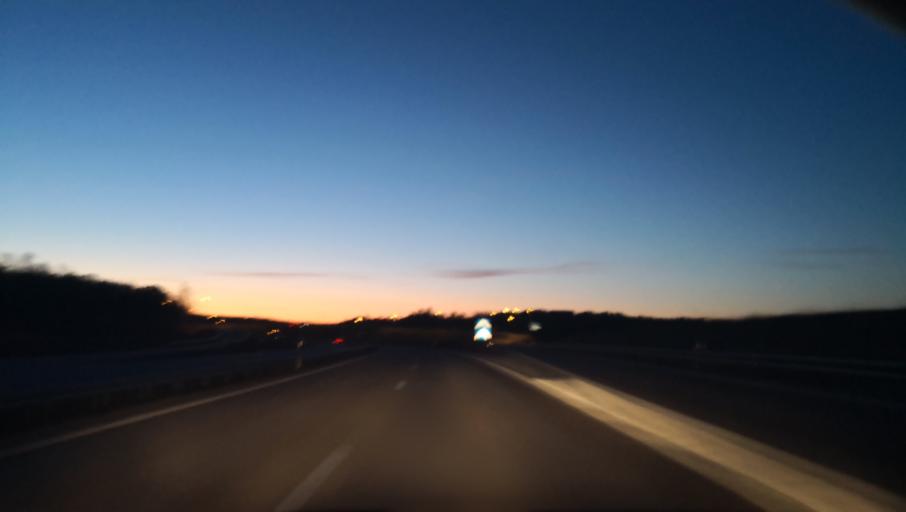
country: SE
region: Stockholm
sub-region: Nynashamns Kommun
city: Osmo
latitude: 58.9412
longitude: 17.9172
